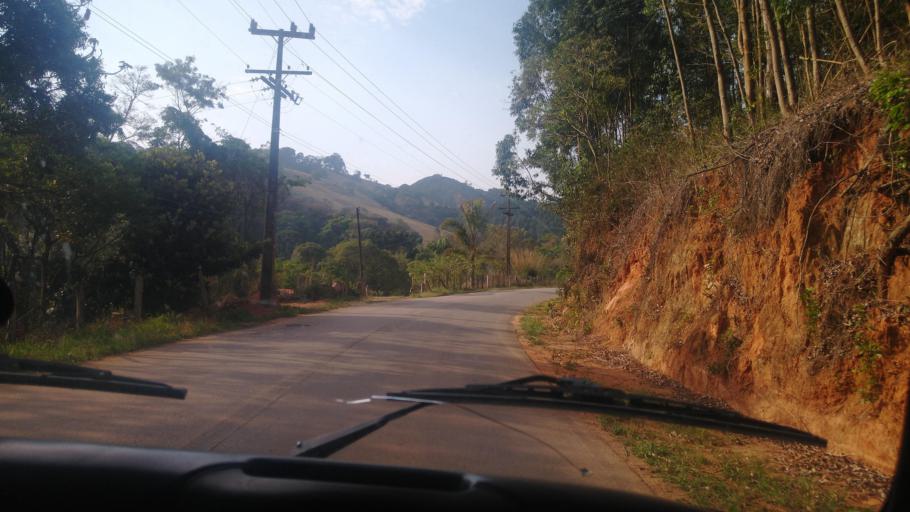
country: BR
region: Minas Gerais
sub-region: Extrema
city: Extrema
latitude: -22.7768
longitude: -46.4402
